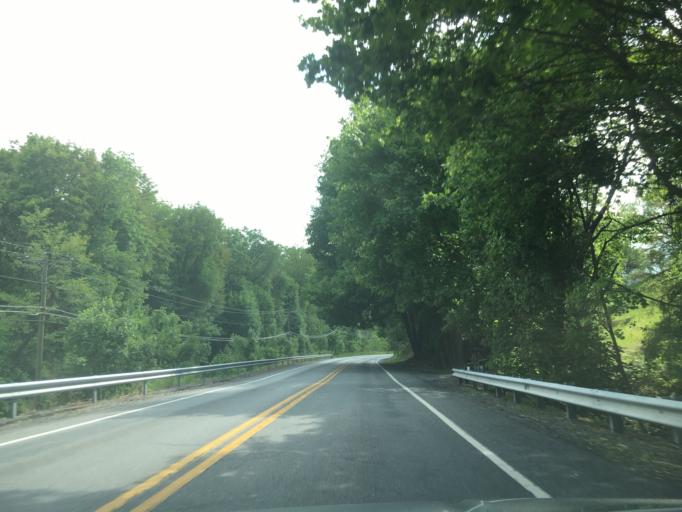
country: US
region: Pennsylvania
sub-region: Northampton County
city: Cherryville
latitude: 40.7474
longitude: -75.5433
